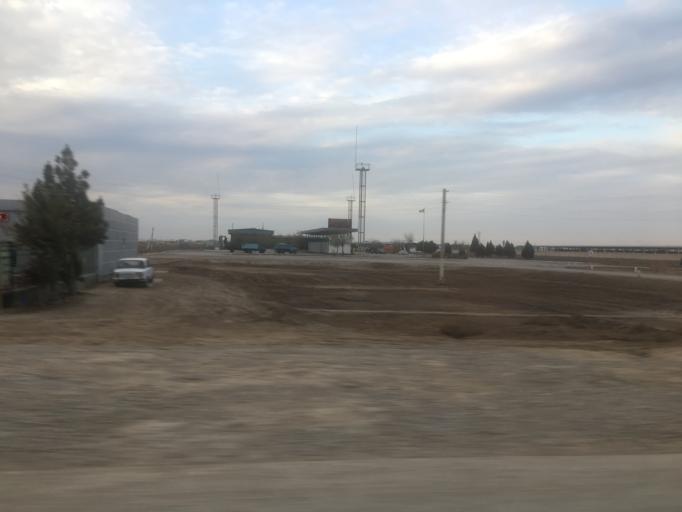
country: TM
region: Ahal
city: Tejen
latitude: 37.3777
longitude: 60.4778
